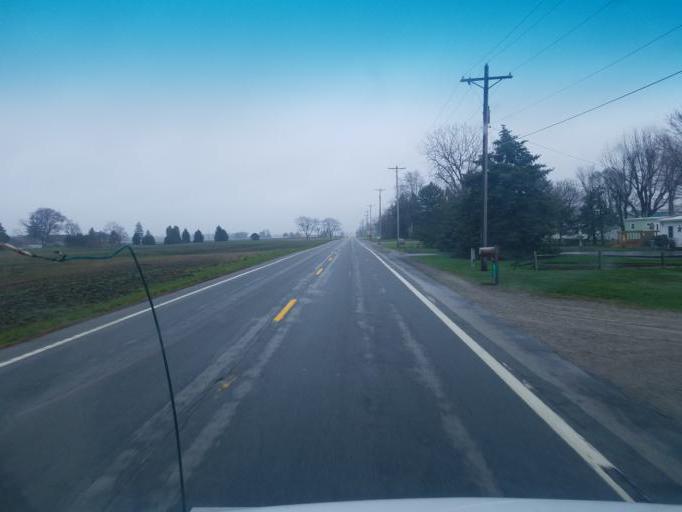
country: US
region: Ohio
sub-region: Wood County
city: Weston
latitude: 41.3722
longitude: -83.7805
